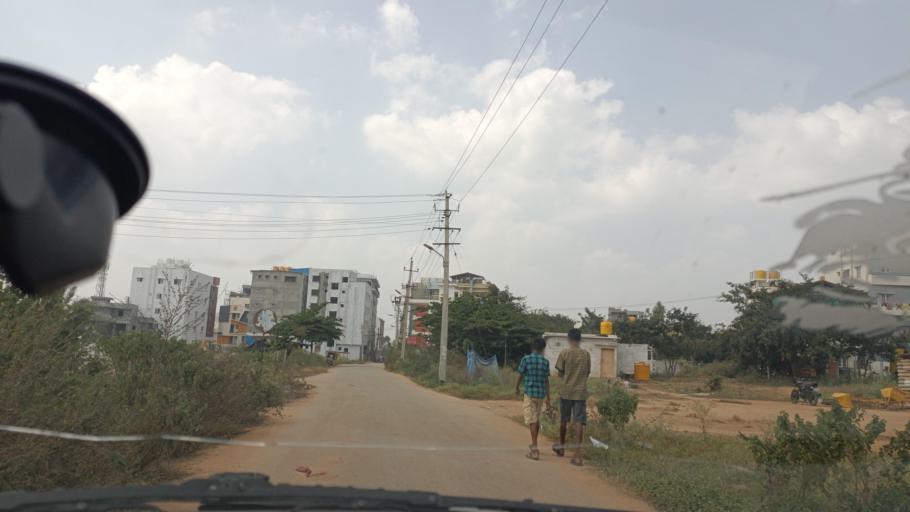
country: IN
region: Karnataka
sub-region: Bangalore Urban
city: Yelahanka
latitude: 13.1629
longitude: 77.6346
